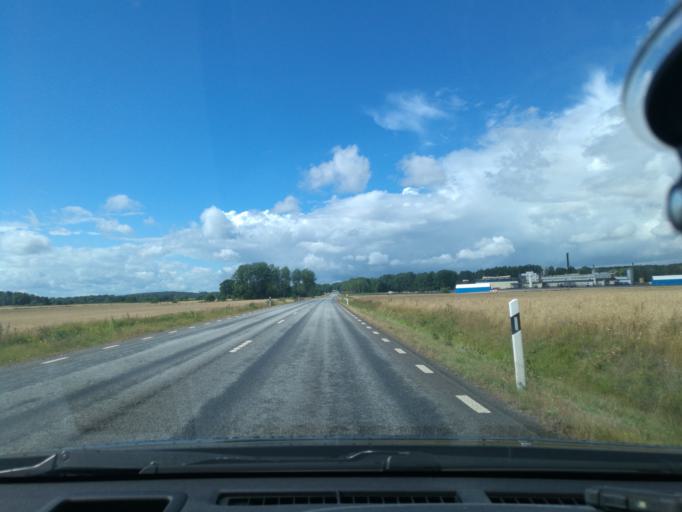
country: SE
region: OErebro
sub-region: Hallsbergs Kommun
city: Skollersta
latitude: 59.1369
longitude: 15.3670
